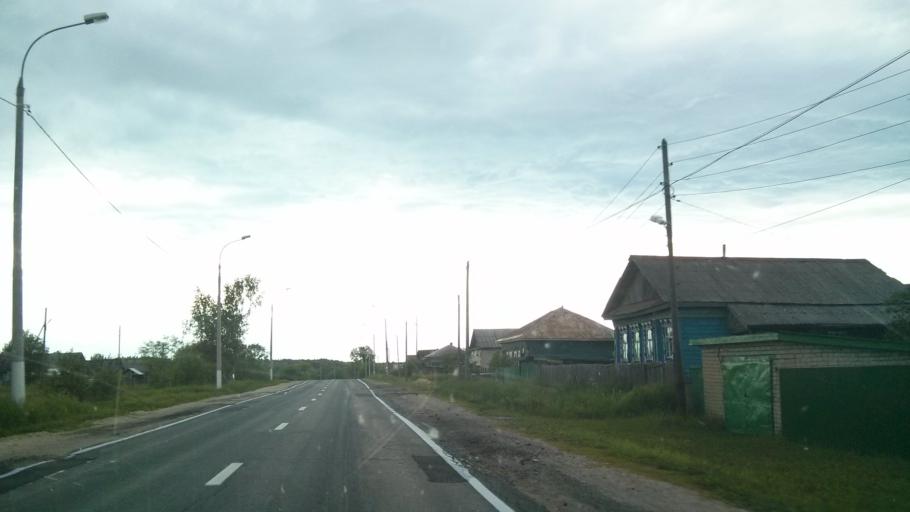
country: RU
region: Nizjnij Novgorod
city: Vacha
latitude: 55.7479
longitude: 42.4928
